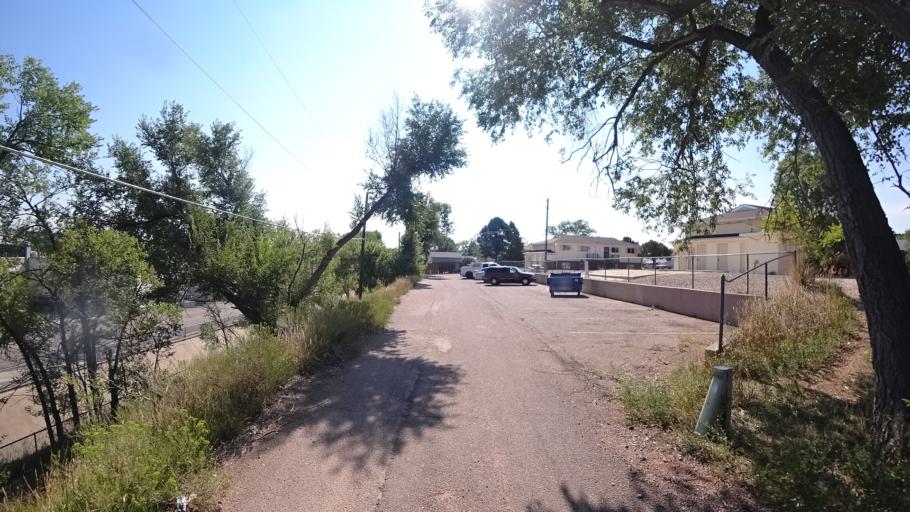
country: US
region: Colorado
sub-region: El Paso County
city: Colorado Springs
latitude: 38.8960
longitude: -104.8435
